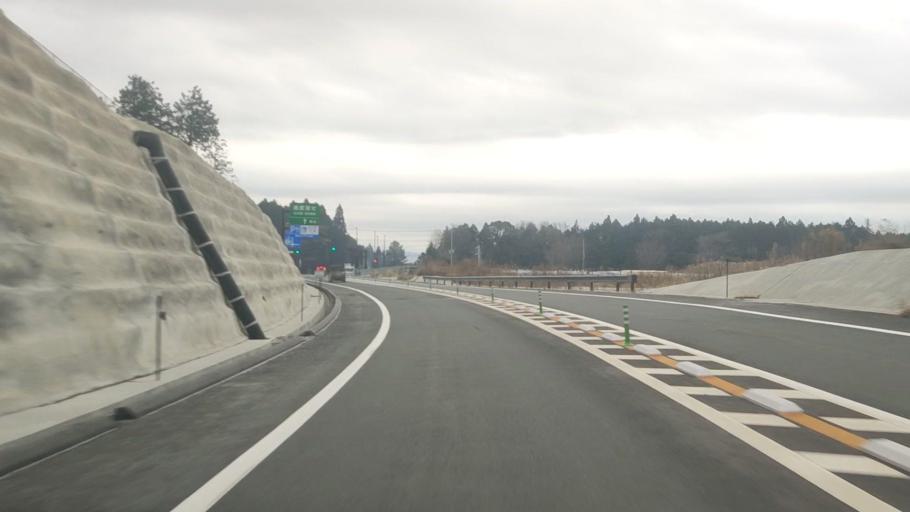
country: JP
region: Kumamoto
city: Ozu
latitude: 32.8894
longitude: 130.8964
